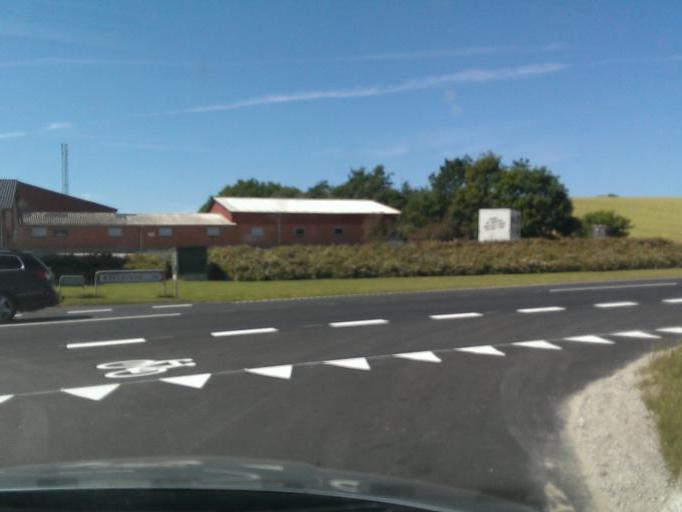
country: DK
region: Central Jutland
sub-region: Arhus Kommune
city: Malling
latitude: 56.0231
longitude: 10.1810
